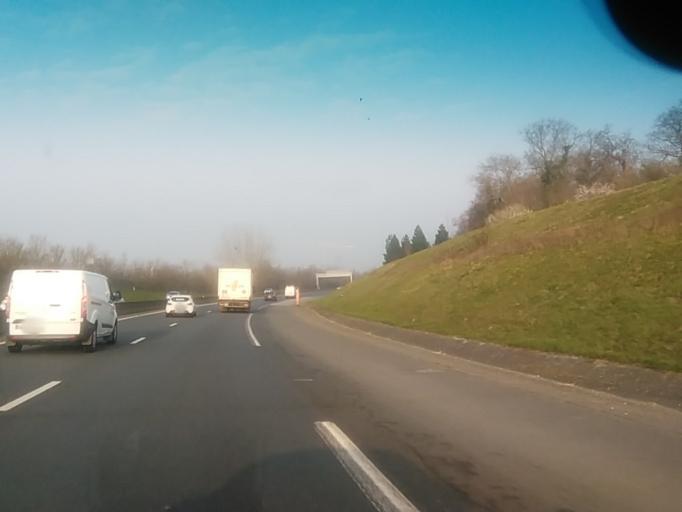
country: FR
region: Lower Normandy
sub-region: Departement du Calvados
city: Fleury-sur-Orne
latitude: 49.1370
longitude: -0.3893
